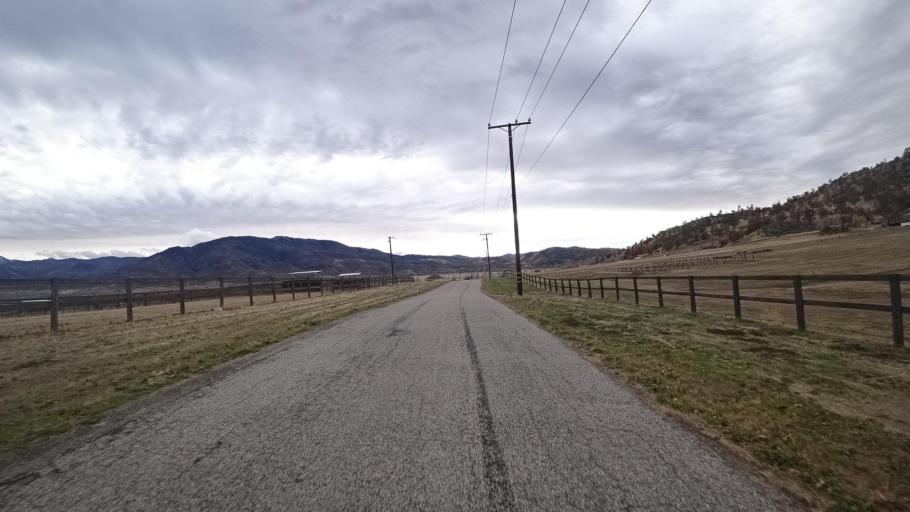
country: US
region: California
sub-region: Kern County
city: Stallion Springs
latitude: 35.1147
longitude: -118.6291
